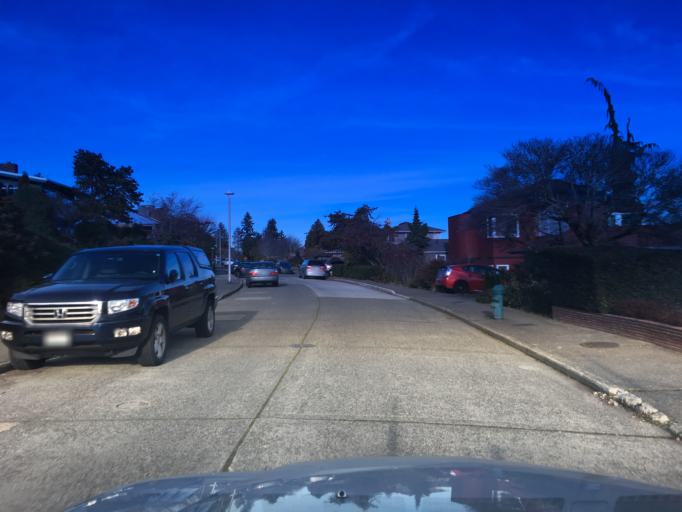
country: US
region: Washington
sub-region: King County
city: Inglewood-Finn Hill
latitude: 47.6807
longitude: -122.2658
